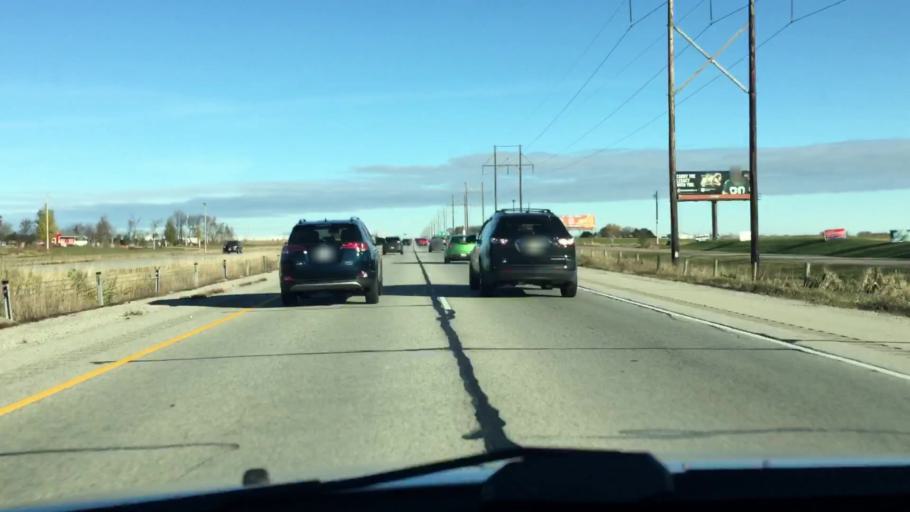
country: US
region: Wisconsin
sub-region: Winnebago County
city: Oshkosh
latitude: 43.9291
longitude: -88.5832
